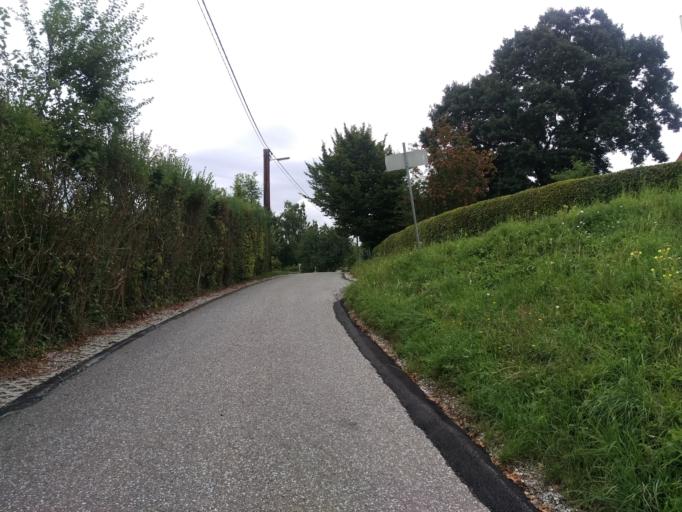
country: AT
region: Styria
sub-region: Politischer Bezirk Graz-Umgebung
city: Raaba
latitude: 47.0509
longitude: 15.4991
